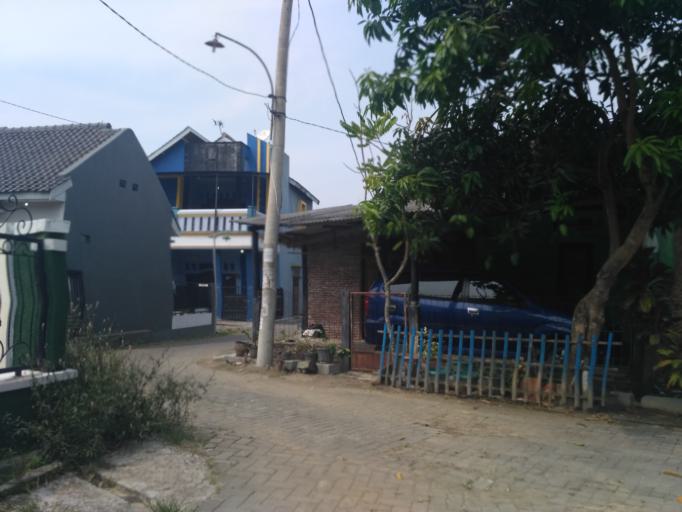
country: ID
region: Central Java
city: Mranggen
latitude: -7.0590
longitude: 110.4672
